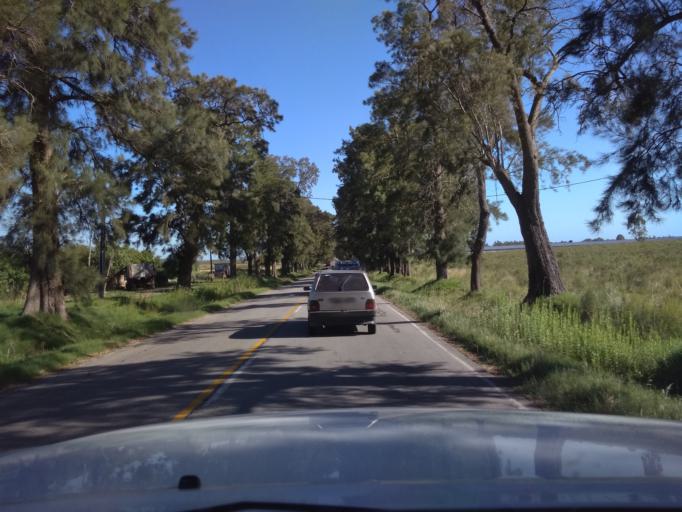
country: UY
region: Canelones
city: San Bautista
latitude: -34.3944
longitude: -55.9596
